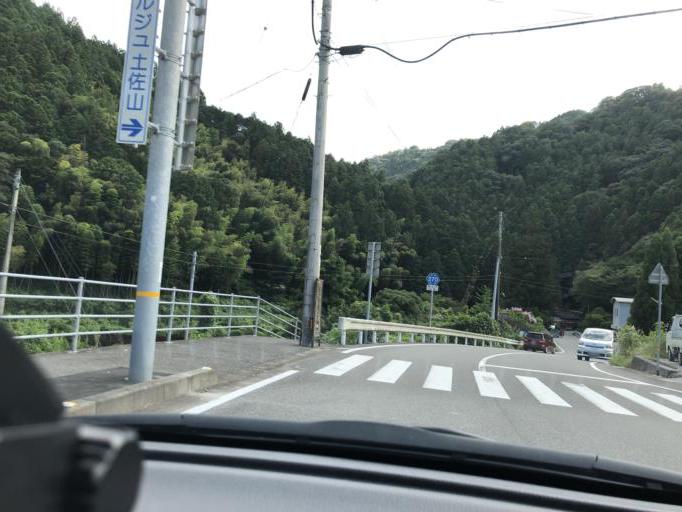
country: JP
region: Kochi
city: Kochi-shi
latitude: 33.6230
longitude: 133.4979
